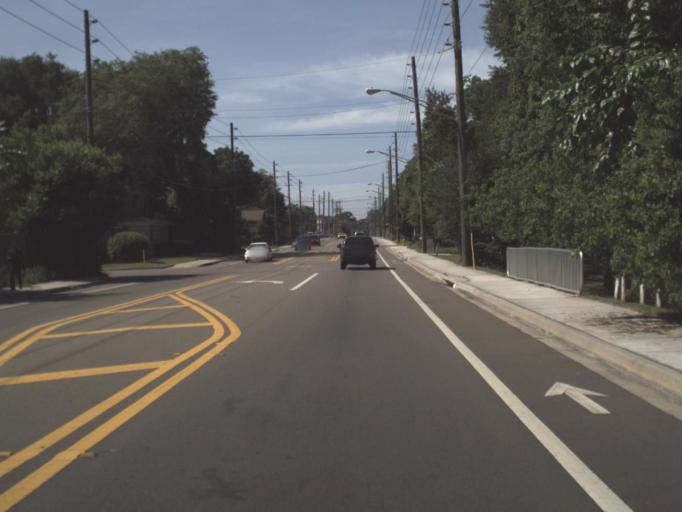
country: US
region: Florida
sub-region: Duval County
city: Jacksonville
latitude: 30.3174
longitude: -81.7054
